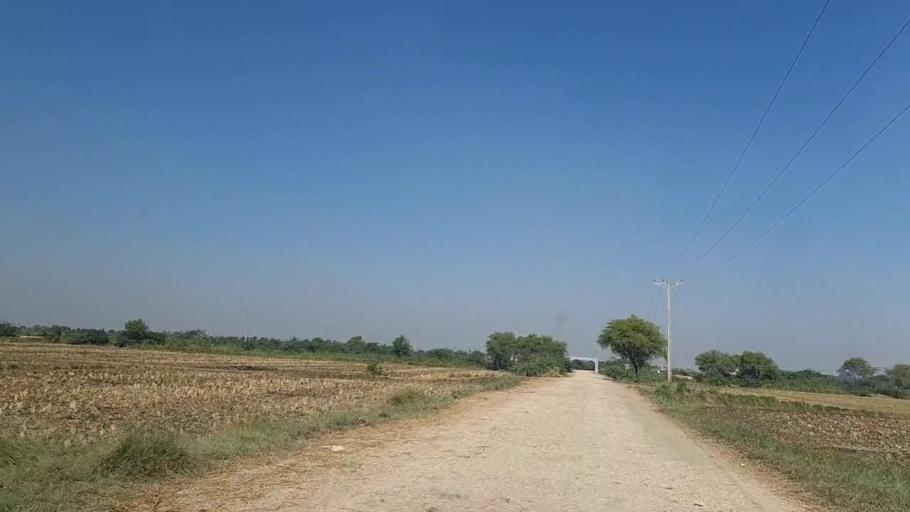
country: PK
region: Sindh
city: Daro Mehar
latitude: 24.7926
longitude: 68.1725
